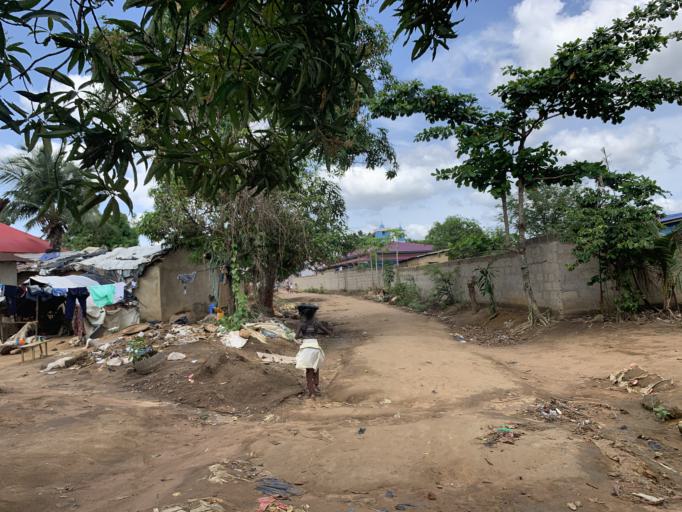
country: SL
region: Western Area
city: Waterloo
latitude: 8.3356
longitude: -13.0450
